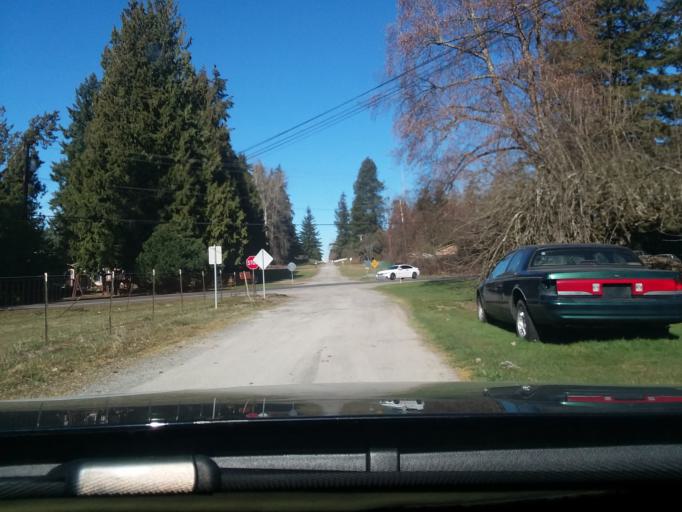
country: US
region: Washington
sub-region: Pierce County
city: Summit
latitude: 47.1629
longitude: -122.3355
